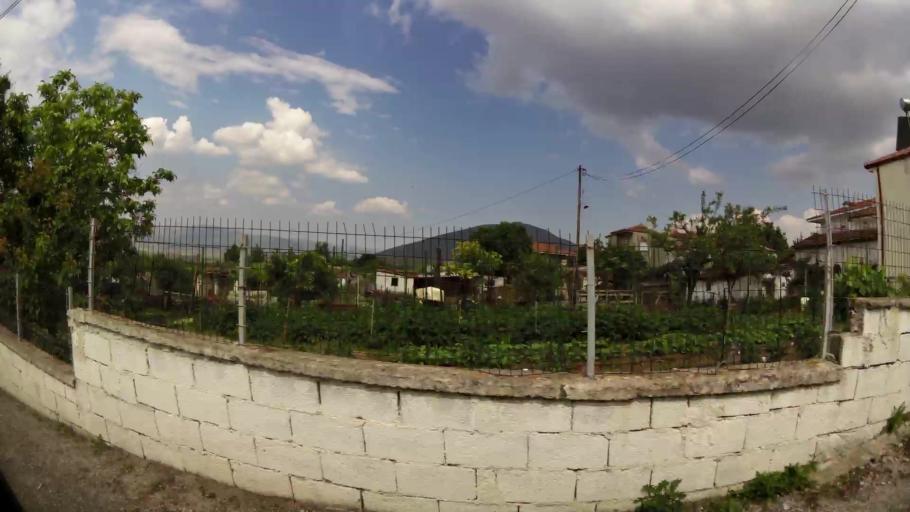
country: GR
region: West Macedonia
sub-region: Nomos Kozanis
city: Koila
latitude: 40.3484
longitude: 21.8423
